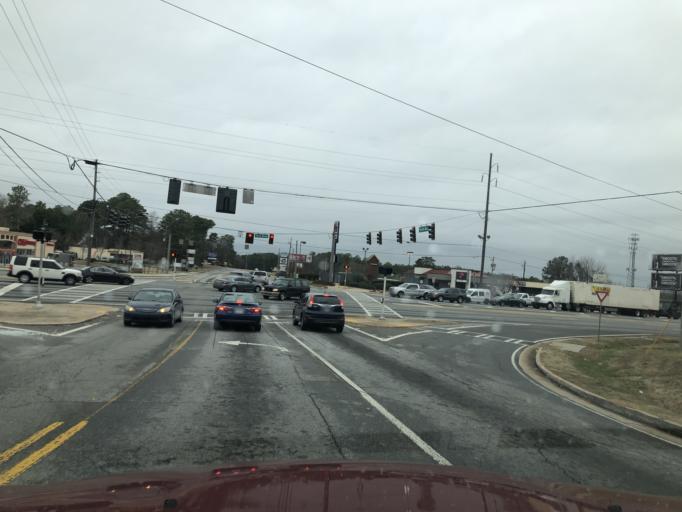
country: US
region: Georgia
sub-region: Clayton County
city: Jonesboro
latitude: 33.5322
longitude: -84.3633
